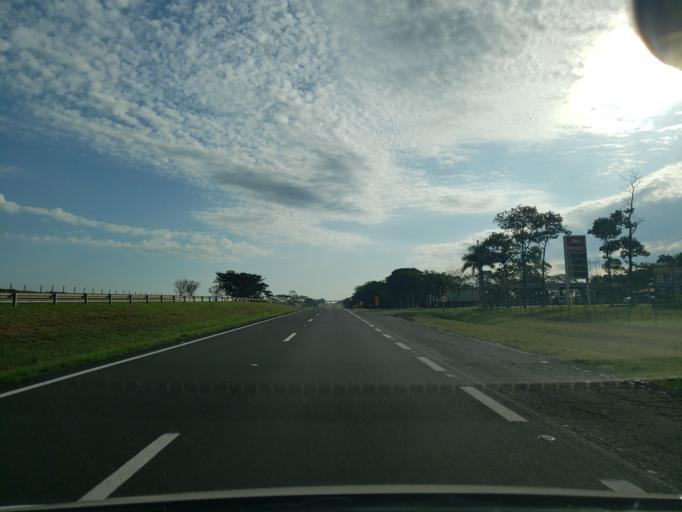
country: BR
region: Sao Paulo
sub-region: Valparaiso
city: Valparaiso
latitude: -21.2059
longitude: -50.7763
